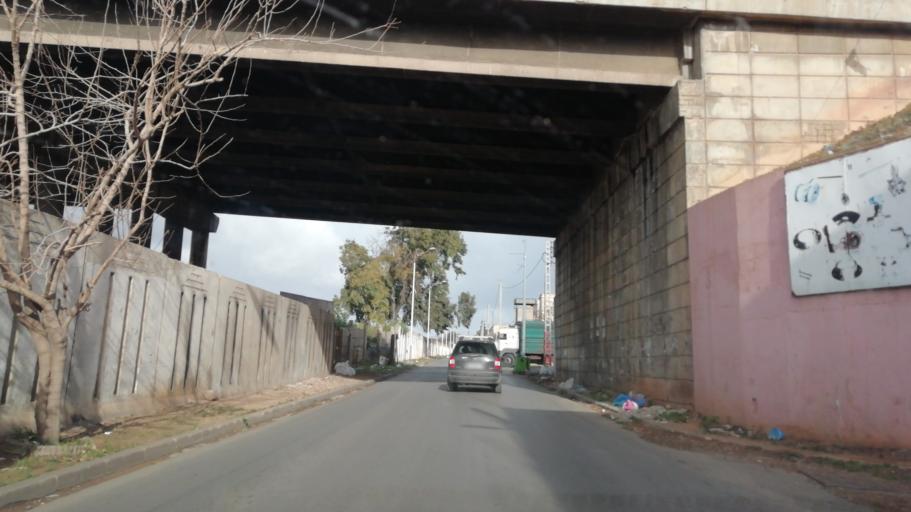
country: DZ
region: Oran
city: Oran
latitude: 35.6849
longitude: -0.6287
